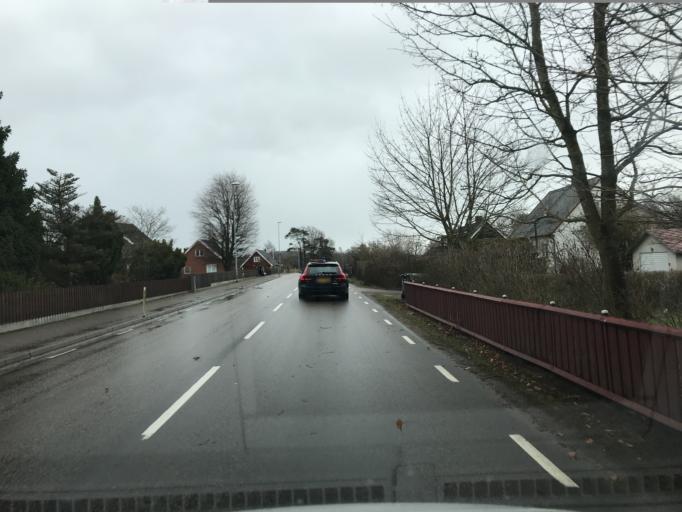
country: SE
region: Skane
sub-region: Klippans Kommun
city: Klippan
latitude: 56.1190
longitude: 13.1750
